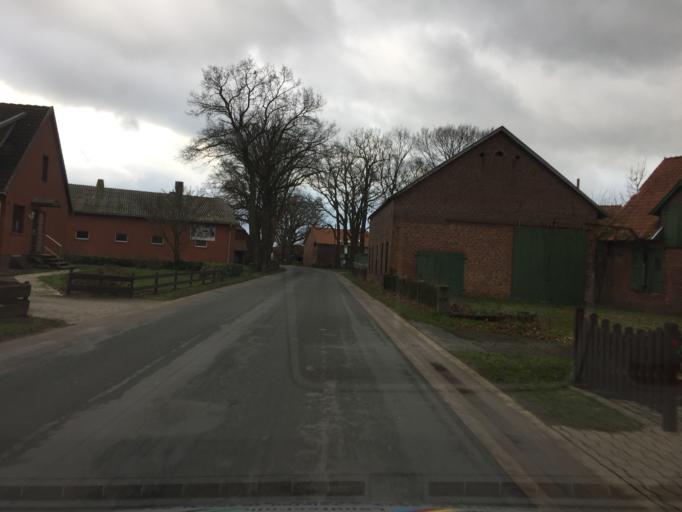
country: DE
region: Lower Saxony
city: Stolzenau
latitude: 52.5204
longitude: 9.0562
